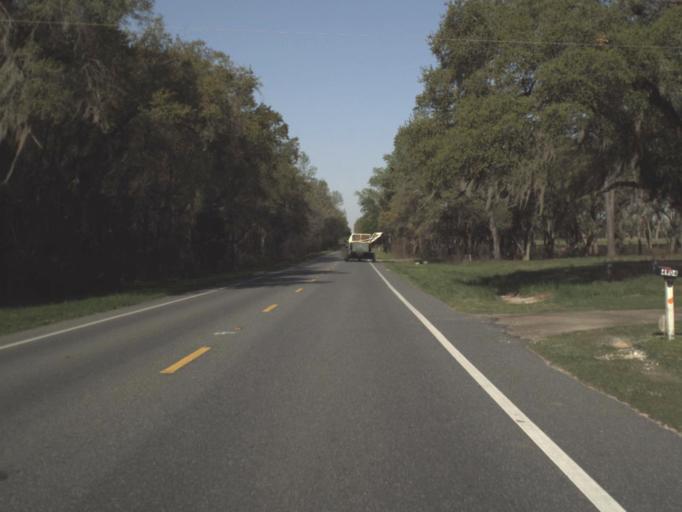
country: US
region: Florida
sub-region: Jackson County
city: Malone
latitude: 30.9590
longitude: -85.1850
